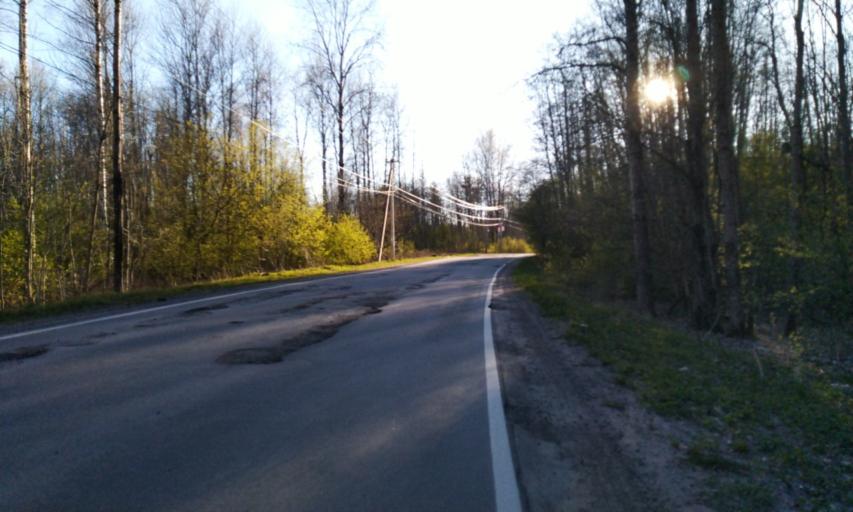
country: RU
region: Leningrad
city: Toksovo
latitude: 60.1389
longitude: 30.5490
